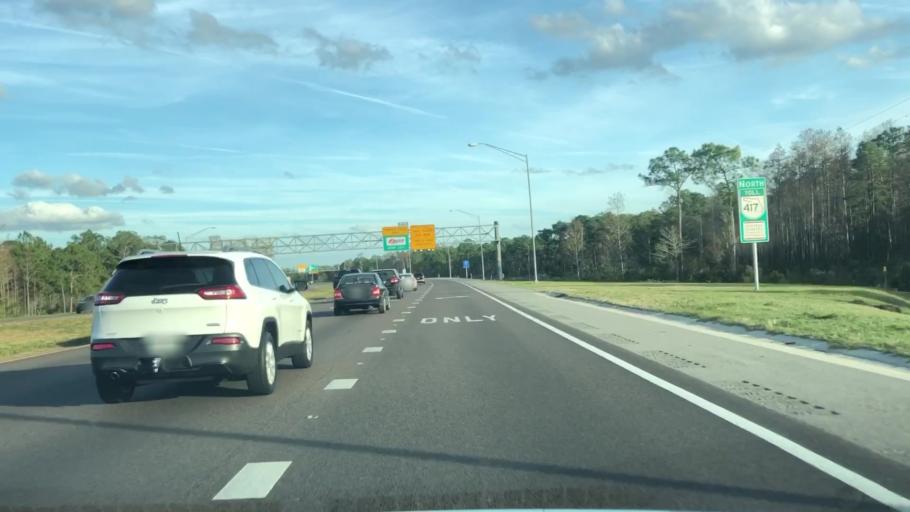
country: US
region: Florida
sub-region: Orange County
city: Hunters Creek
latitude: 28.3549
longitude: -81.4725
